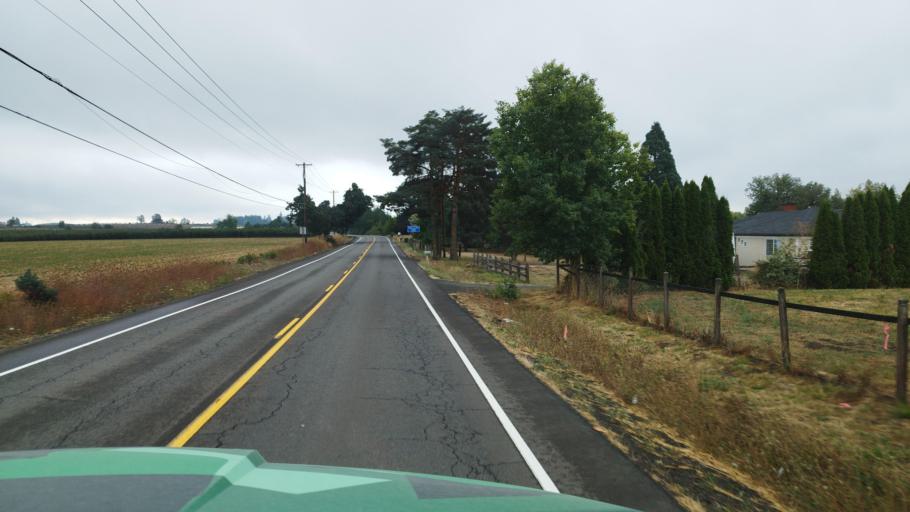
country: US
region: Oregon
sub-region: Yamhill County
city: Yamhill
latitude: 45.3336
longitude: -123.1853
